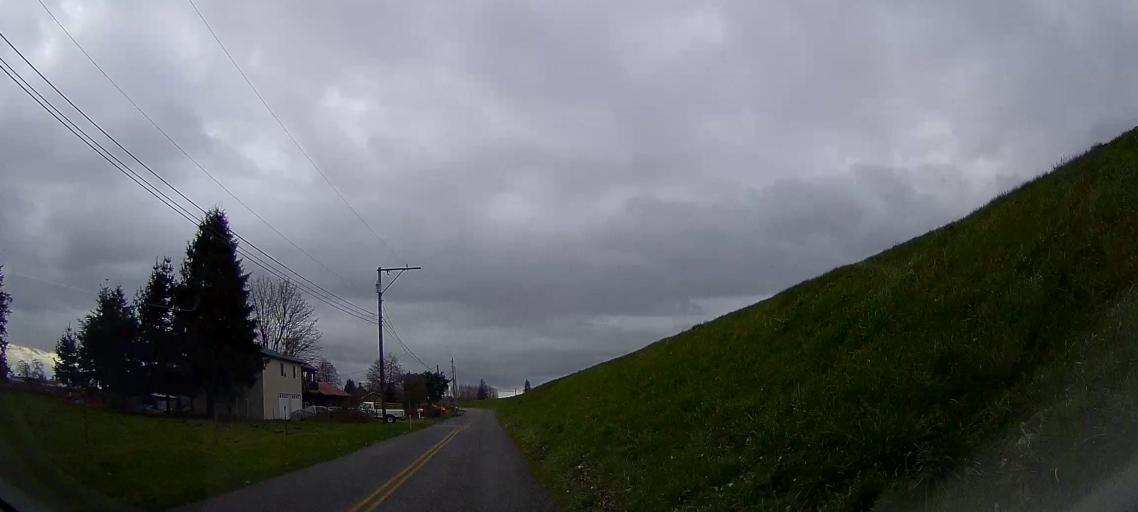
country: US
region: Washington
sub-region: Skagit County
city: Mount Vernon
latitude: 48.4453
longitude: -122.3674
